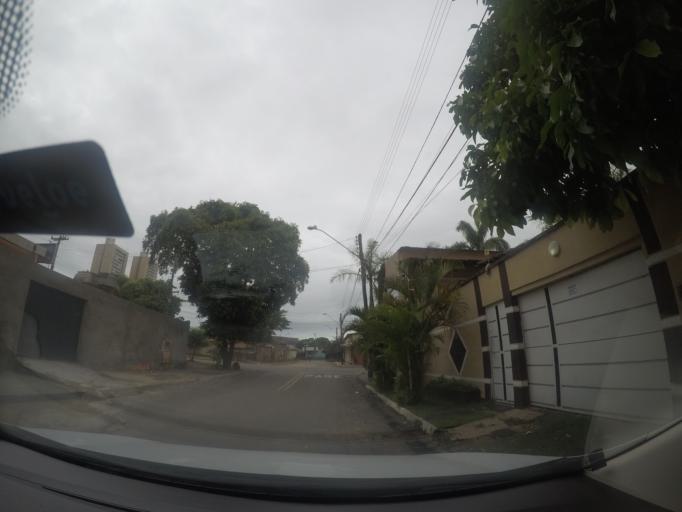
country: BR
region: Goias
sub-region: Goiania
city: Goiania
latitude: -16.6643
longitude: -49.3085
